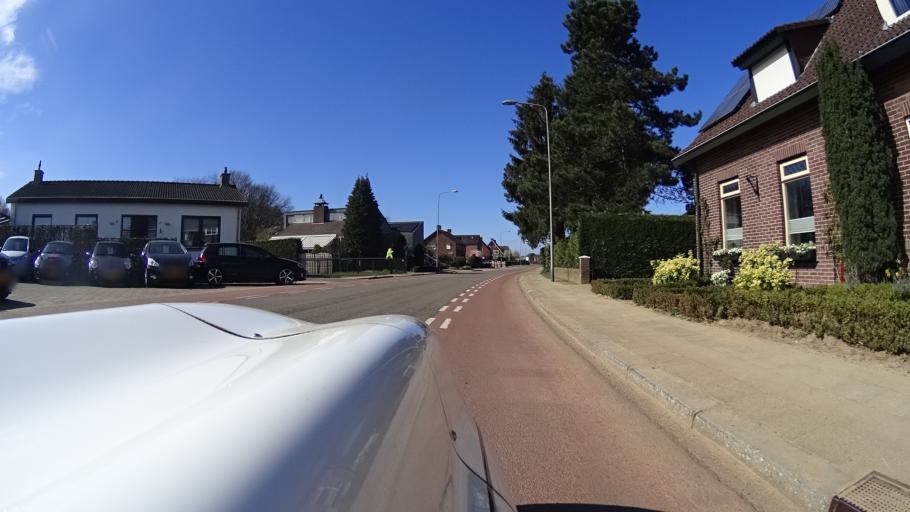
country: NL
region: Limburg
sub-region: Gemeente Bergen
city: Wellerlooi
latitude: 51.5301
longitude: 6.1067
